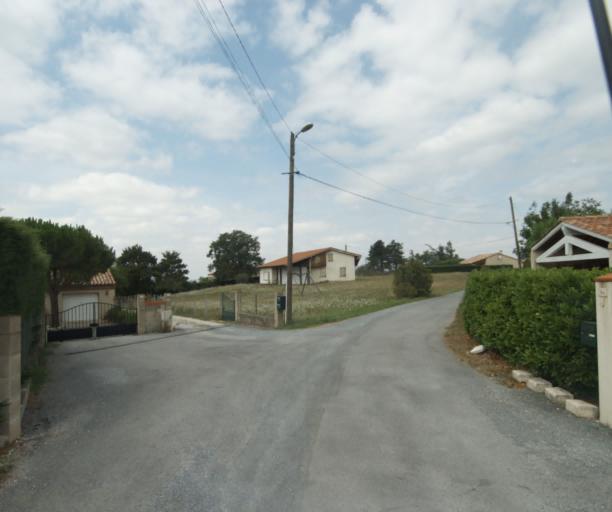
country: FR
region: Midi-Pyrenees
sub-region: Departement de la Haute-Garonne
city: Revel
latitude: 43.4475
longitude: 2.0342
